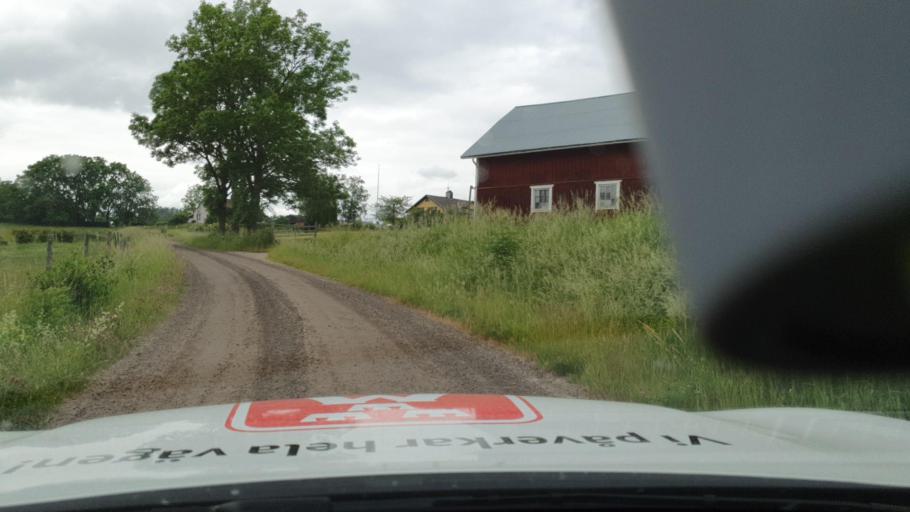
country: SE
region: Vaestra Goetaland
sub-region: Hjo Kommun
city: Hjo
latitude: 58.1752
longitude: 14.1753
